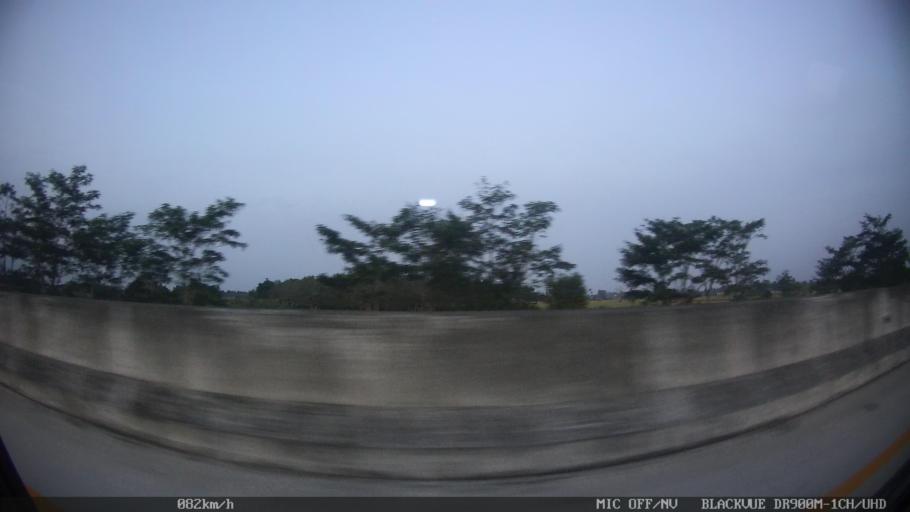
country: ID
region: Lampung
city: Sidorejo
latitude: -5.6280
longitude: 105.5658
